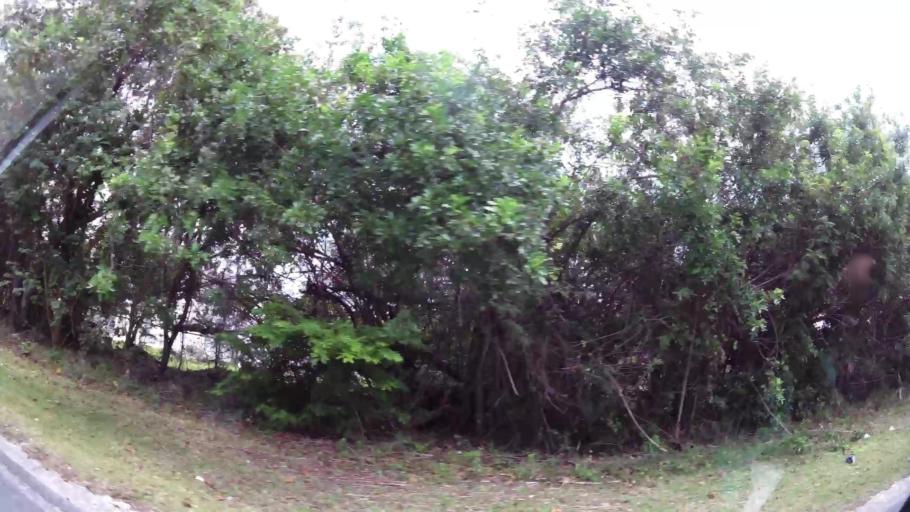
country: BS
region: Freeport
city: Lucaya
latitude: 26.5208
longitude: -78.6499
